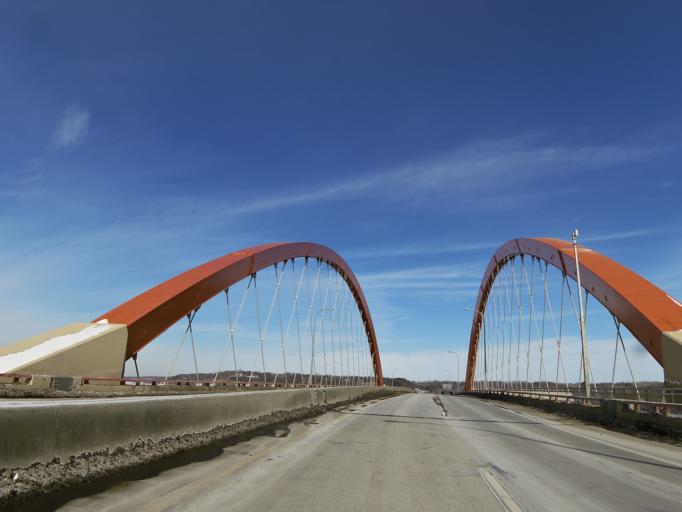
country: US
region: Minnesota
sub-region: Dakota County
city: Hastings
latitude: 44.7453
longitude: -92.8529
